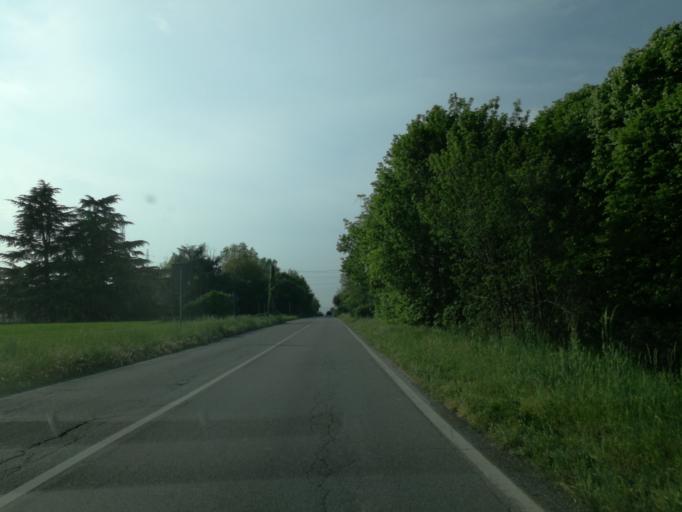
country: IT
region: Lombardy
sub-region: Provincia di Lecco
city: Verderio Superiore
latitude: 45.6571
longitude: 9.4568
